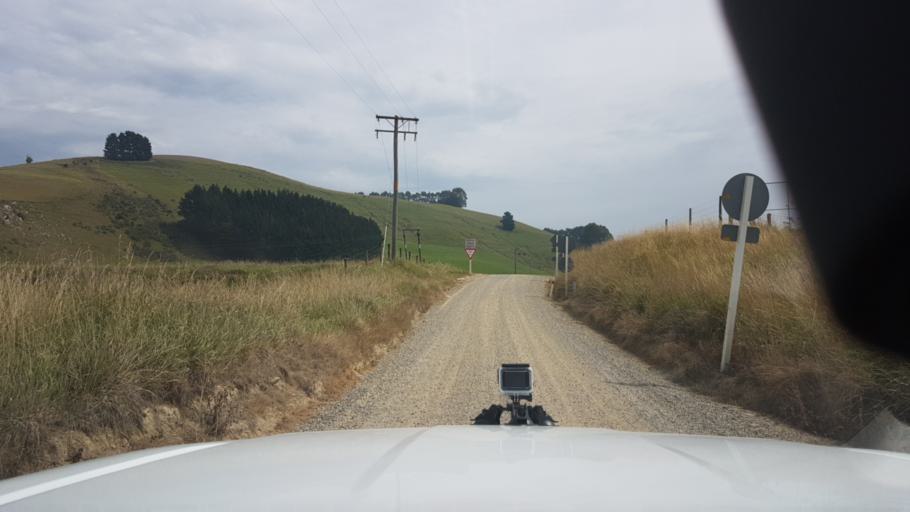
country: NZ
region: Otago
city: Oamaru
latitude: -45.0330
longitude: 170.9505
